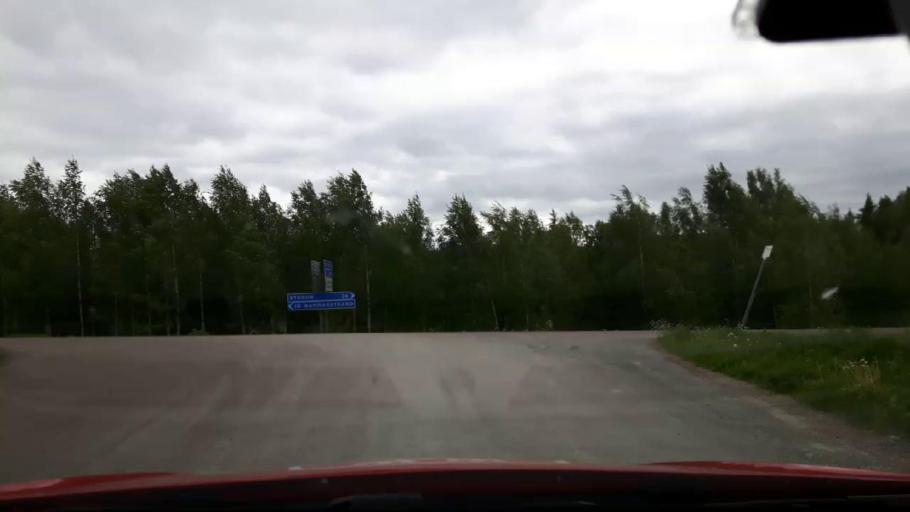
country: SE
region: Jaemtland
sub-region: Ragunda Kommun
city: Hammarstrand
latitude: 63.1539
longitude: 16.2426
